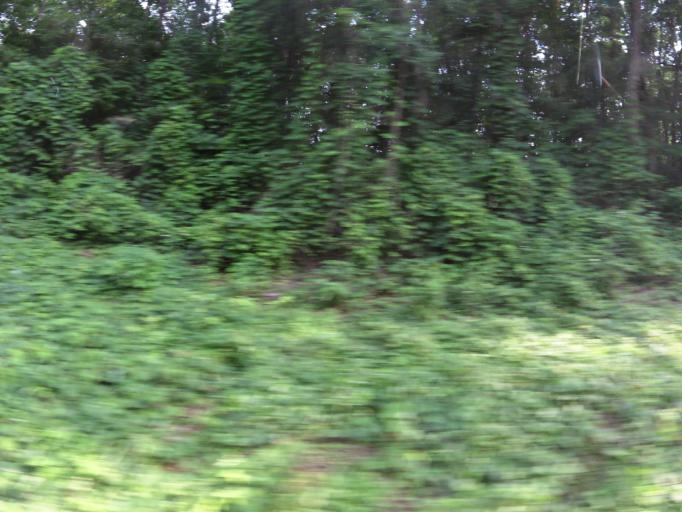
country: US
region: Tennessee
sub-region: Humphreys County
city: McEwen
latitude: 36.1032
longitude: -87.6765
